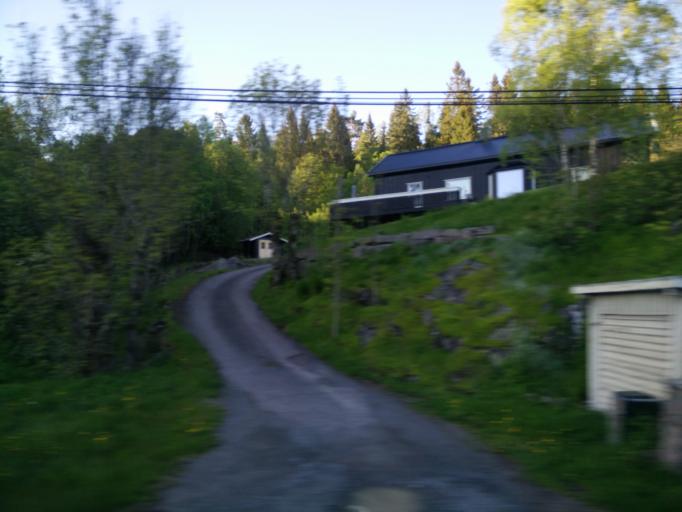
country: NO
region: Akershus
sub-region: Baerum
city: Skui
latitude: 59.9633
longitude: 10.3546
